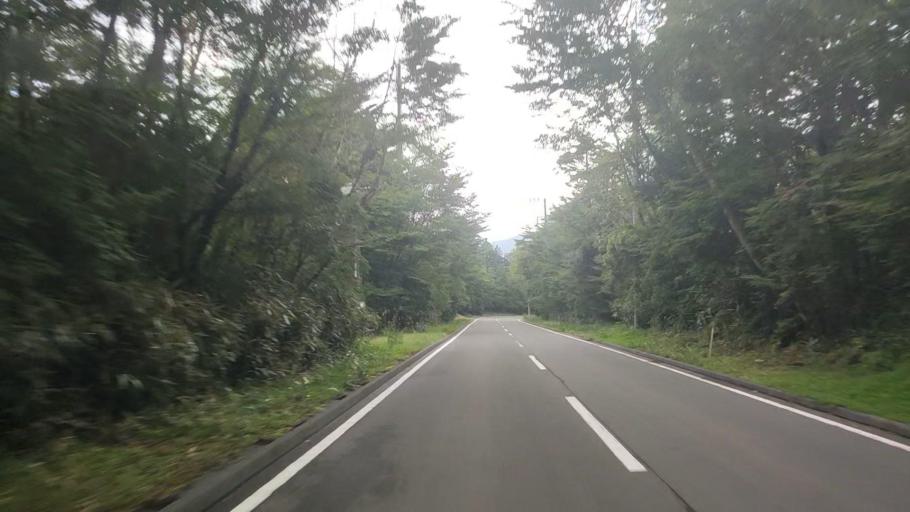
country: JP
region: Shizuoka
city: Gotemba
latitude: 35.2726
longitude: 138.7974
